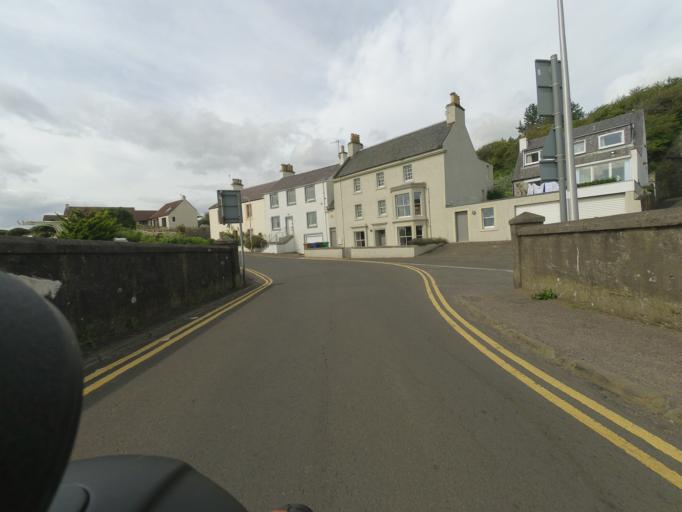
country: GB
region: Scotland
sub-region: Fife
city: Lundin Links
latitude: 56.2122
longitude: -2.9420
